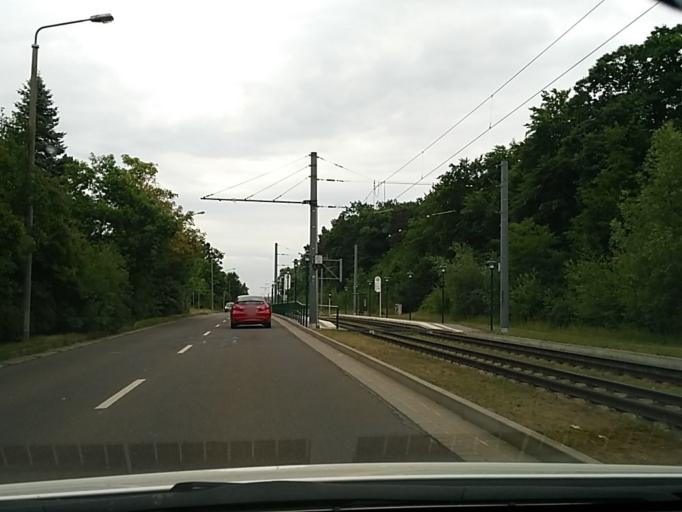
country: DE
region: Saxony-Anhalt
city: Halle Neustadt
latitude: 51.5045
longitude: 11.9285
